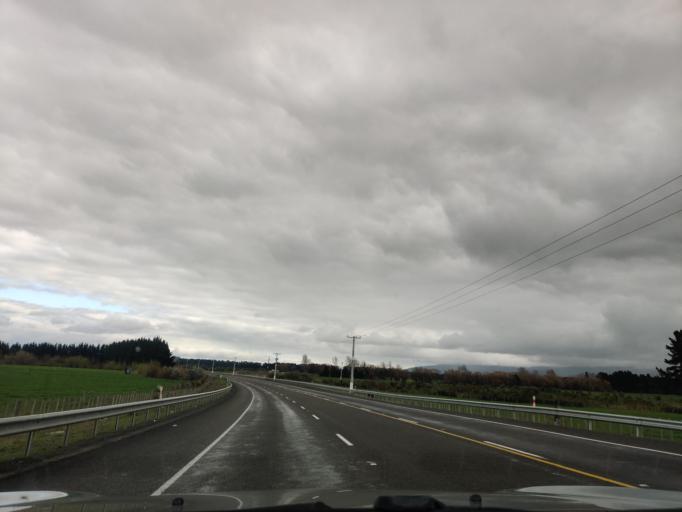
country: NZ
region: Manawatu-Wanganui
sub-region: Palmerston North City
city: Palmerston North
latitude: -40.2351
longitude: 176.0505
